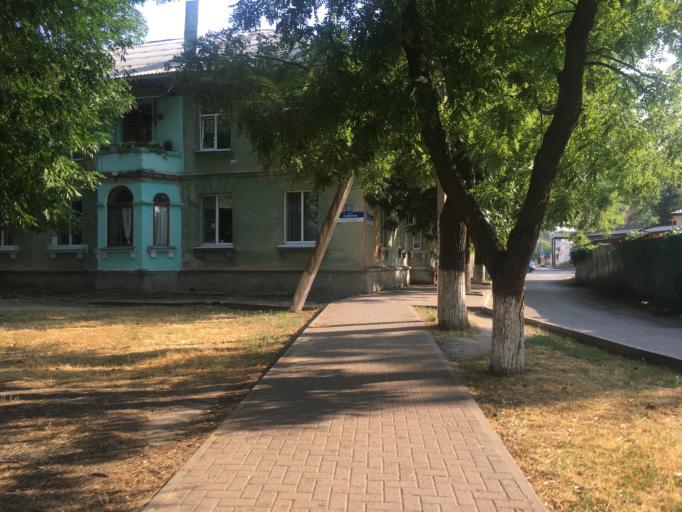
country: RU
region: Krasnodarskiy
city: Yeysk
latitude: 46.7133
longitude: 38.2762
